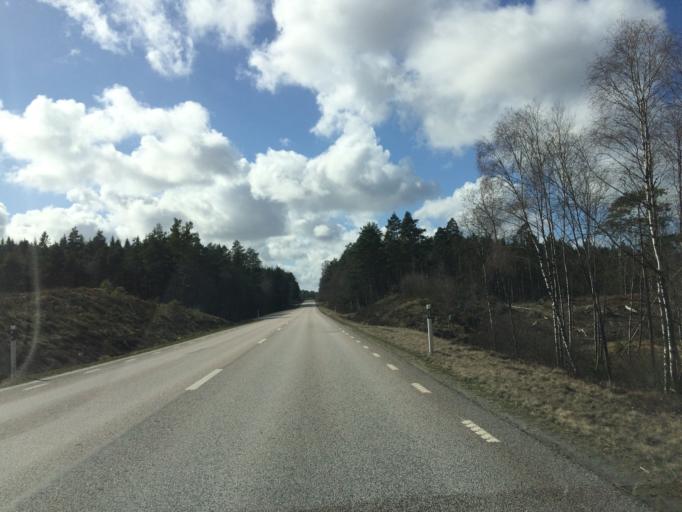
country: SE
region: Halland
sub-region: Laholms Kommun
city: Knared
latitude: 56.4929
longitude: 13.4407
